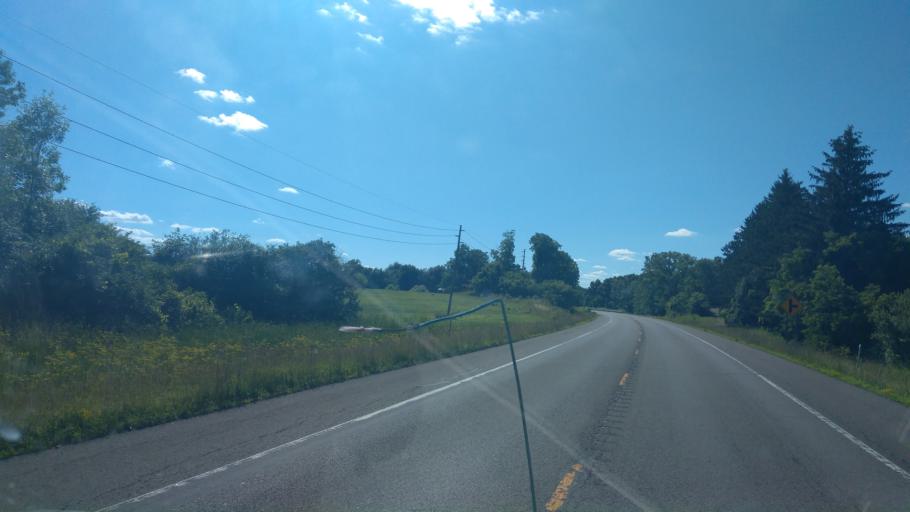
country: US
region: New York
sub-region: Seneca County
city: Seneca Falls
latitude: 42.9585
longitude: -76.8238
